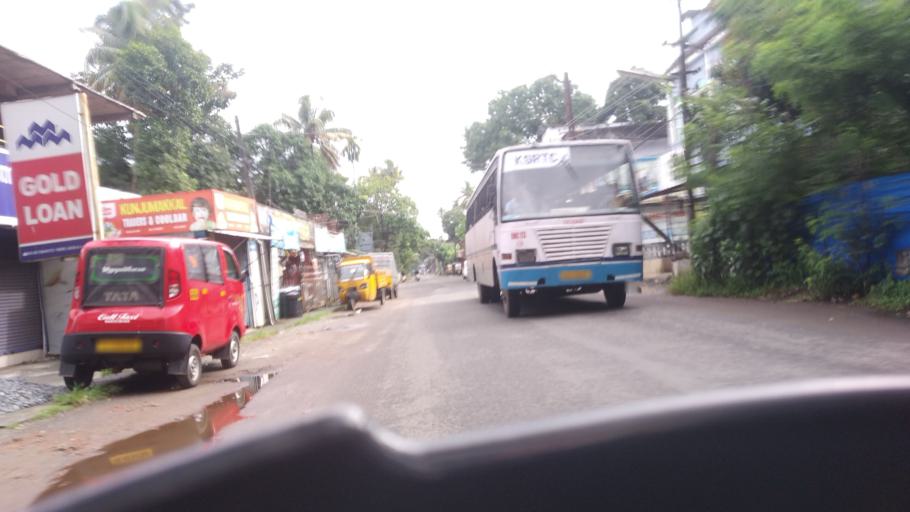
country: IN
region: Kerala
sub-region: Ernakulam
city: Elur
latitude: 10.0874
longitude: 76.2086
